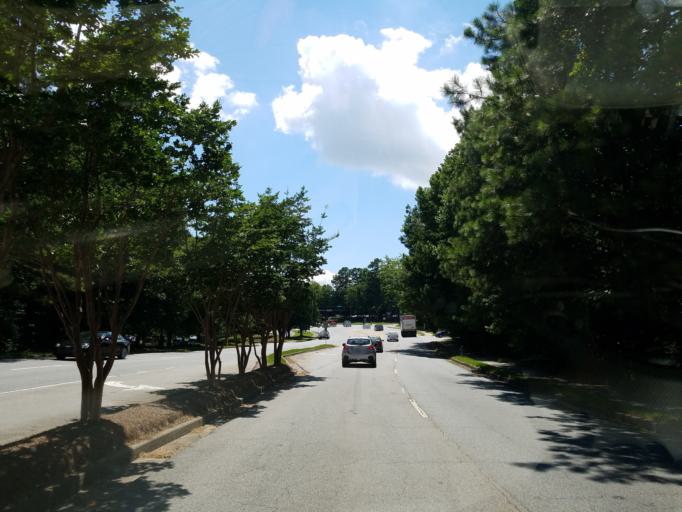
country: US
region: Georgia
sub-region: Fulton County
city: Alpharetta
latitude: 34.0849
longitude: -84.2715
